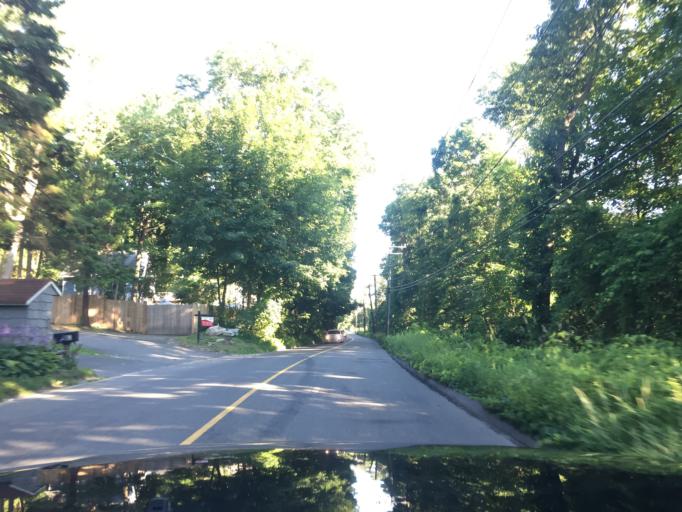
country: US
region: Connecticut
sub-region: Fairfield County
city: Bethel
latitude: 41.4099
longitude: -73.4038
